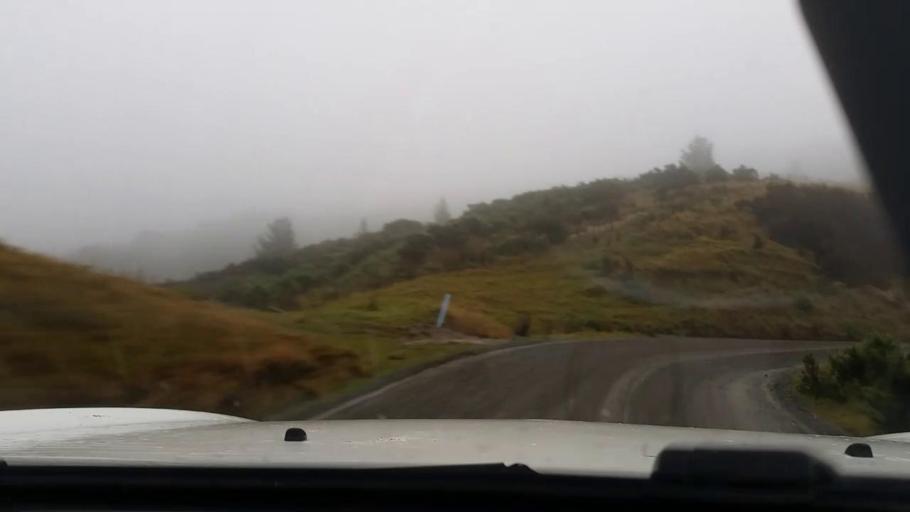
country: NZ
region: Wellington
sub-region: Masterton District
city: Masterton
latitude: -41.2473
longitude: 175.8783
